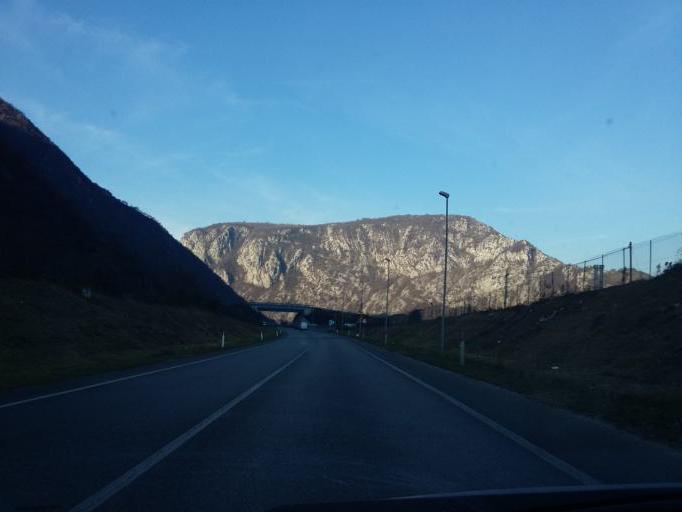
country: IT
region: Lombardy
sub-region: Provincia di Brescia
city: Vobarno
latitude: 45.6378
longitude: 10.4955
